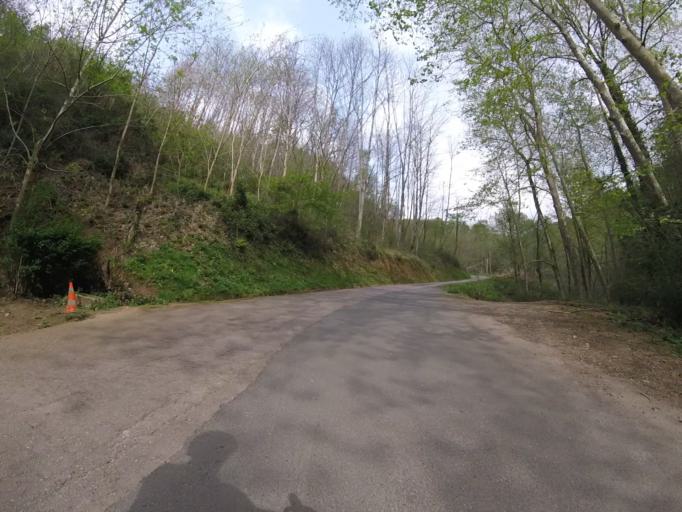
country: ES
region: Basque Country
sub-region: Provincia de Guipuzcoa
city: Anoeta
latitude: 43.1654
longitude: -2.0785
